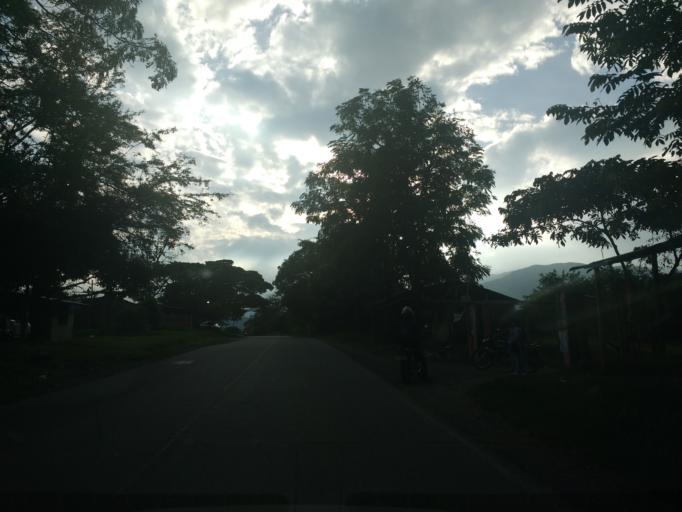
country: CO
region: Cauca
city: Caloto
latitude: 3.0615
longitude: -76.3685
